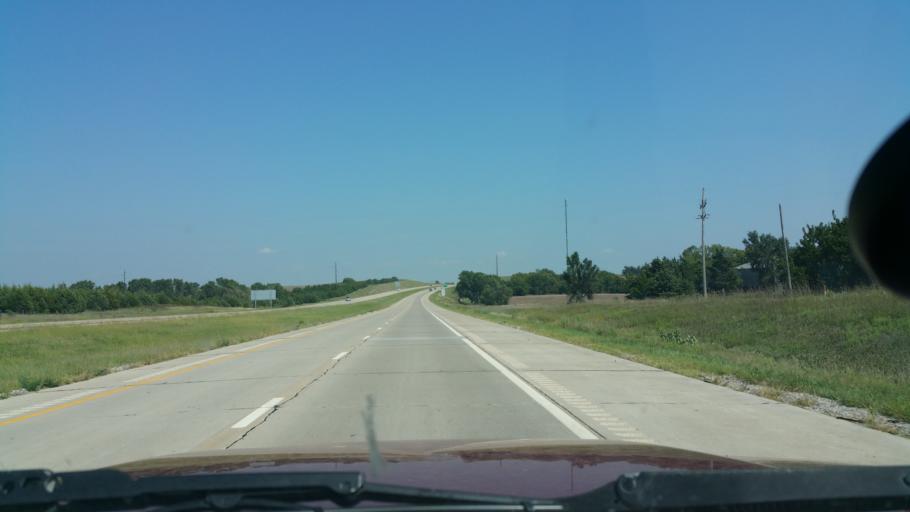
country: US
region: Kansas
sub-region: Dickinson County
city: Abilene
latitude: 38.9419
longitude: -97.2058
